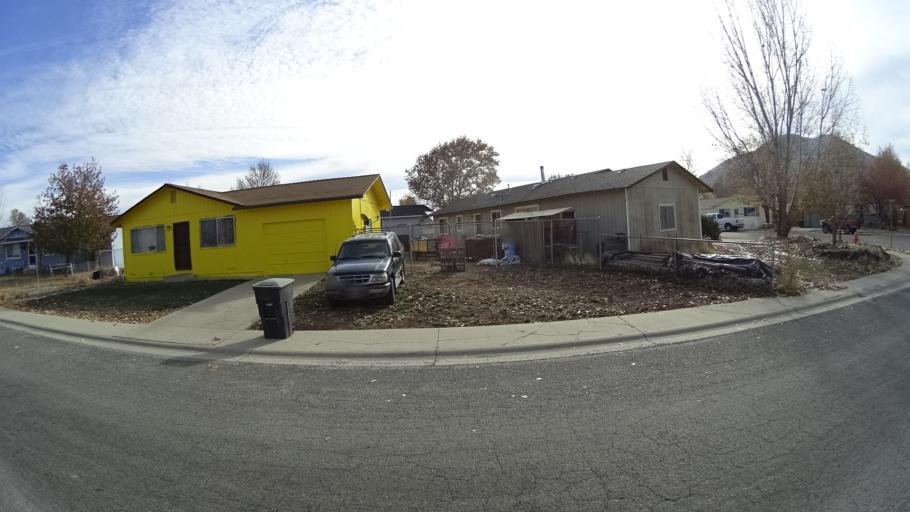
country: US
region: California
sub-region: Siskiyou County
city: Montague
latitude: 41.7266
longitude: -122.5183
